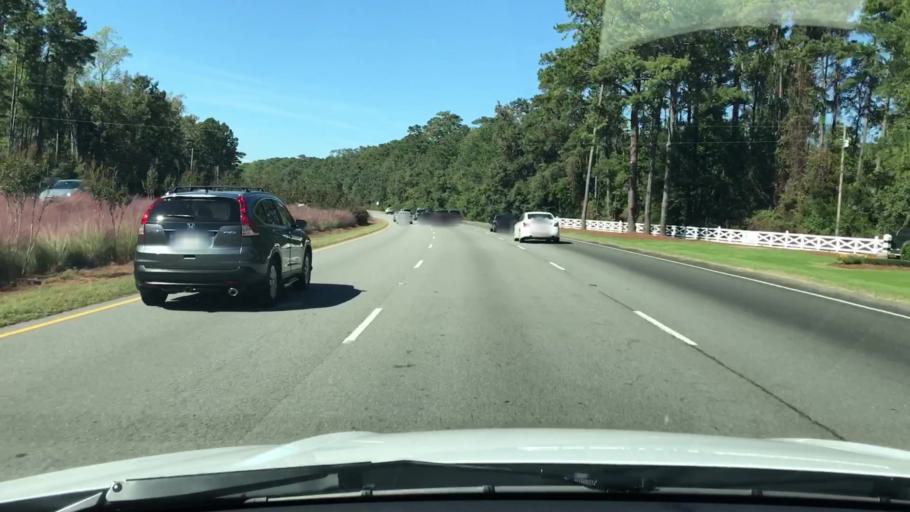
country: US
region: South Carolina
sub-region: Beaufort County
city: Bluffton
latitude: 32.2795
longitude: -80.8734
